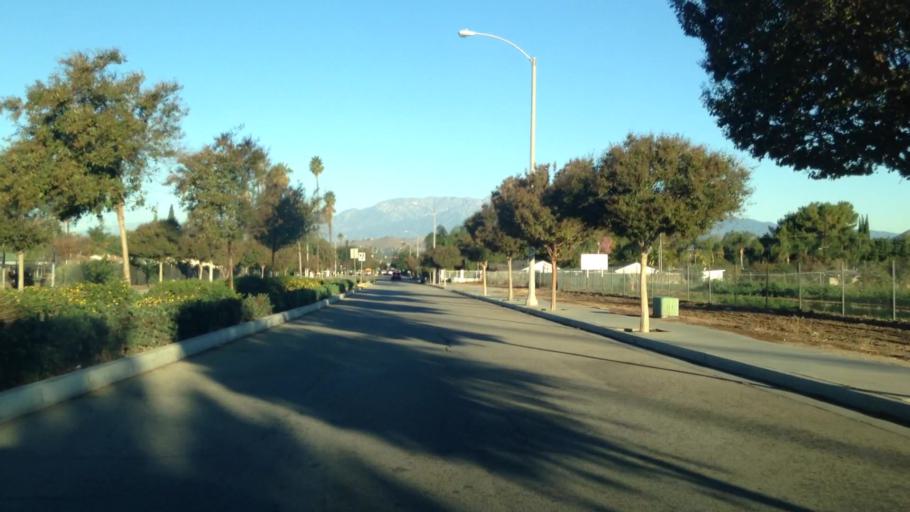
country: US
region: California
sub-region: Riverside County
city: Riverside
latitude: 33.9264
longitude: -117.3971
